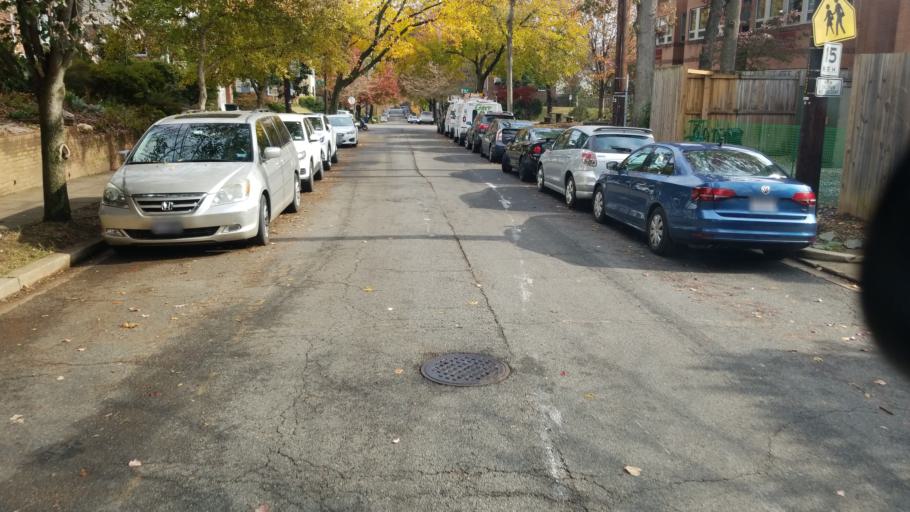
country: US
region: Maryland
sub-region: Montgomery County
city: Chevy Chase Village
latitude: 38.9471
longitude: -77.0706
